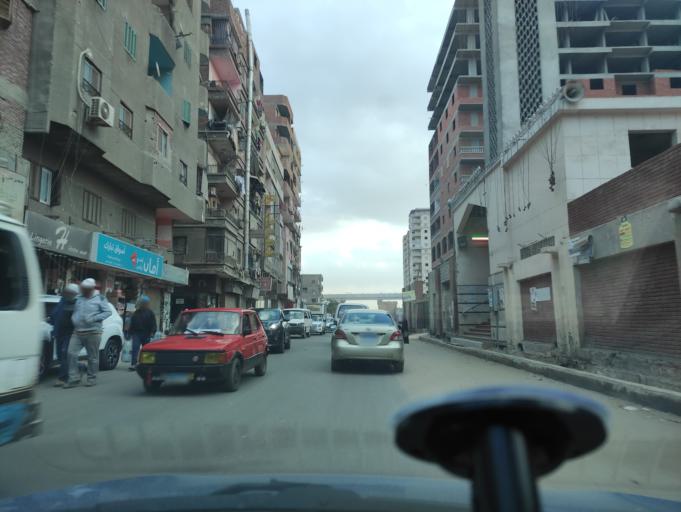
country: EG
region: Muhafazat al Qalyubiyah
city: Al Khankah
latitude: 30.1315
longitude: 31.3607
